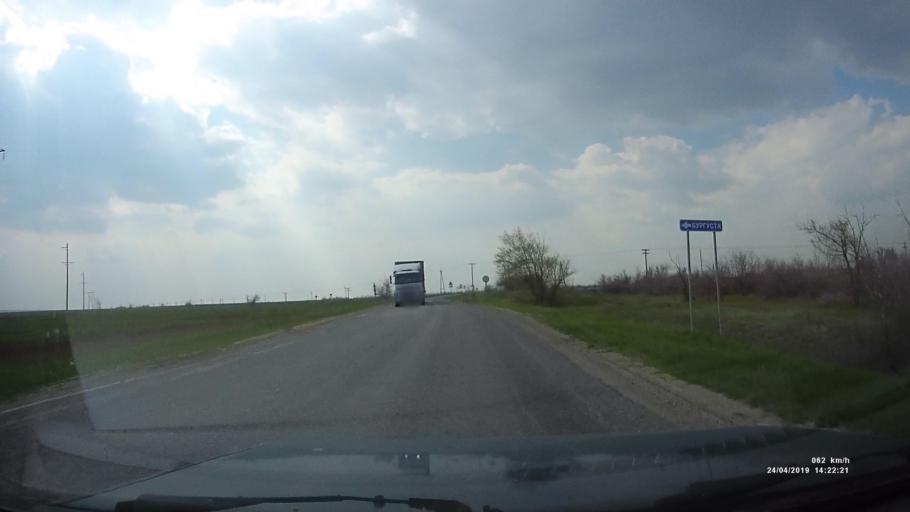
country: RU
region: Kalmykiya
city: Arshan'
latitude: 46.3171
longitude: 44.1243
